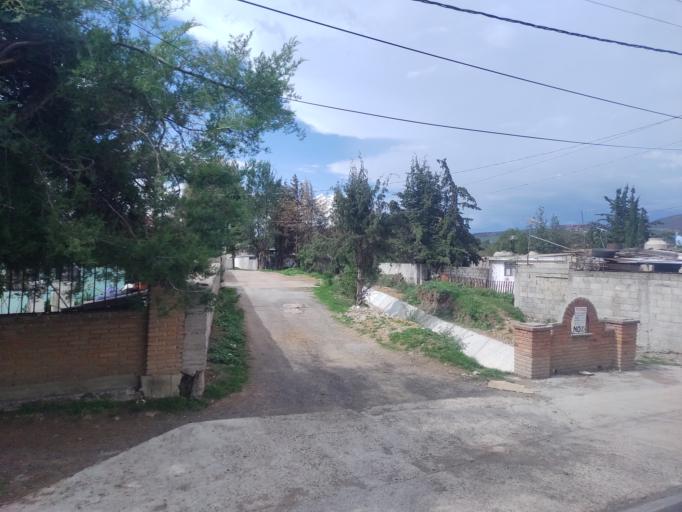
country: MX
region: Mexico
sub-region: Aculco
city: El Colorado
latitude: 20.1042
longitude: -99.7304
